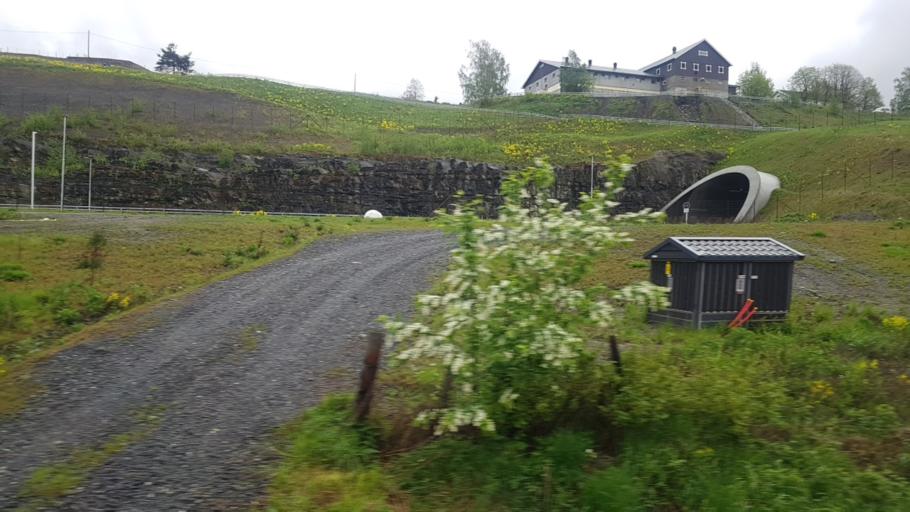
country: NO
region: Oppland
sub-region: Sor-Fron
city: Hundorp
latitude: 61.5600
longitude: 9.9281
